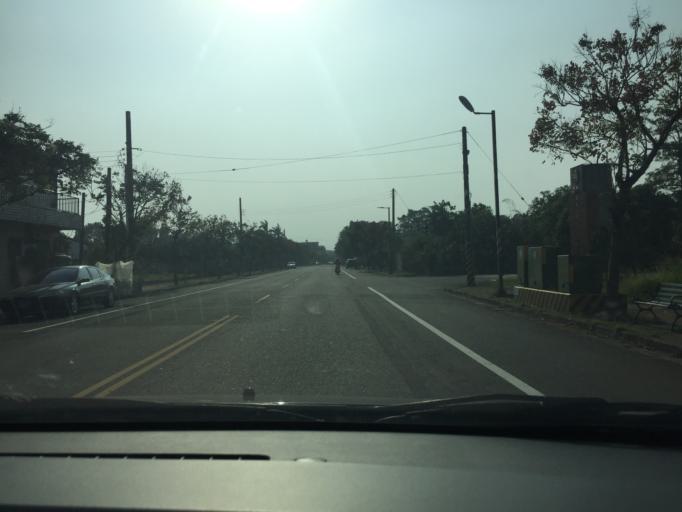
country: TW
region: Taiwan
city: Xinying
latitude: 23.1882
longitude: 120.2660
